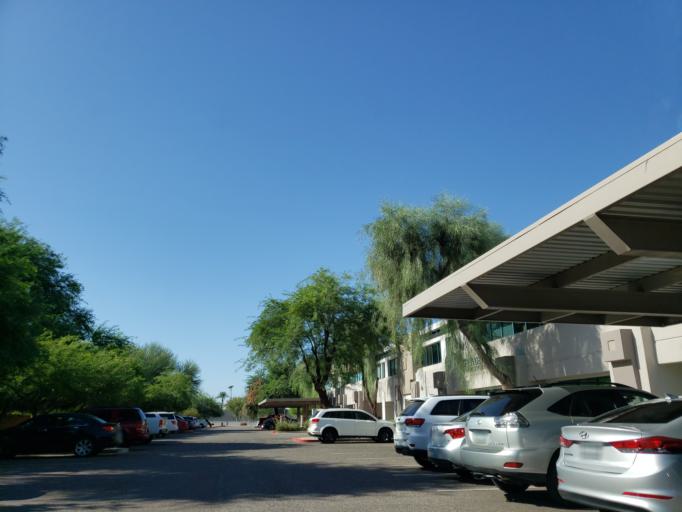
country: US
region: Arizona
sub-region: Maricopa County
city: Paradise Valley
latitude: 33.5874
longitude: -111.9244
